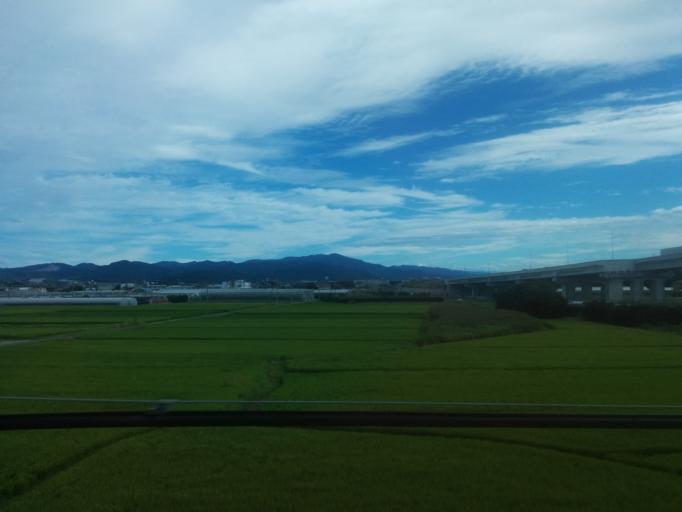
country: JP
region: Aichi
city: Kozakai-cho
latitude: 34.7974
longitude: 137.3306
